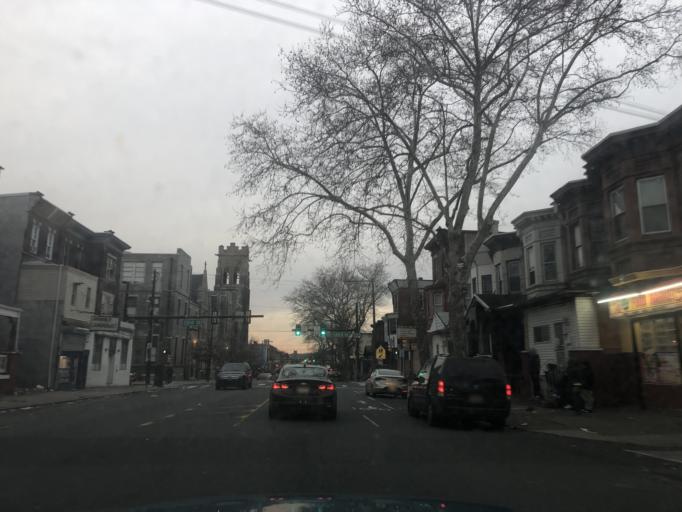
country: US
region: Pennsylvania
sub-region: Philadelphia County
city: Philadelphia
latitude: 39.9958
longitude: -75.1685
